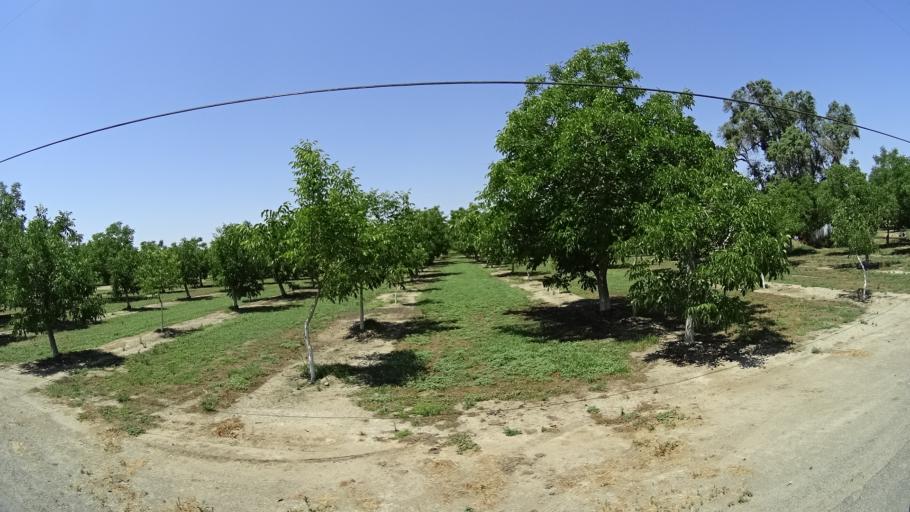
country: US
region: California
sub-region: Fresno County
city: Laton
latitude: 36.3991
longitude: -119.7368
